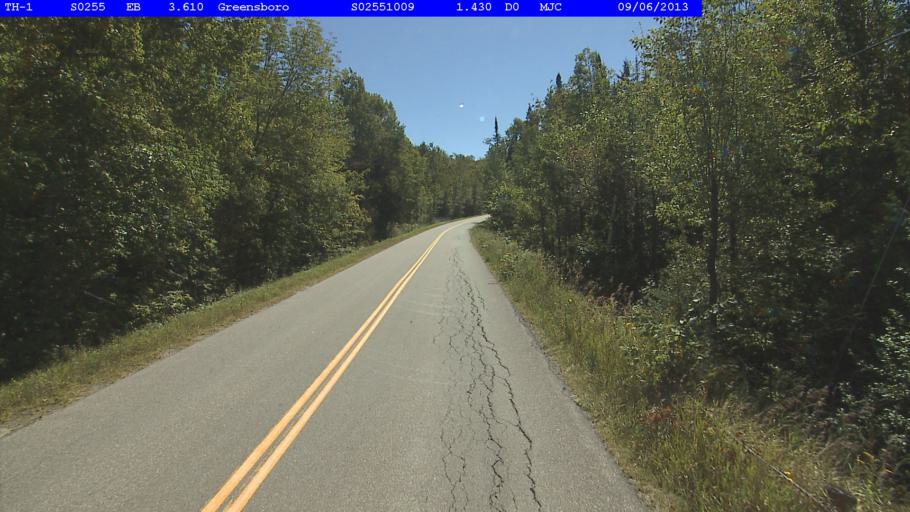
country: US
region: Vermont
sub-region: Caledonia County
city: Hardwick
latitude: 44.6206
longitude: -72.3284
